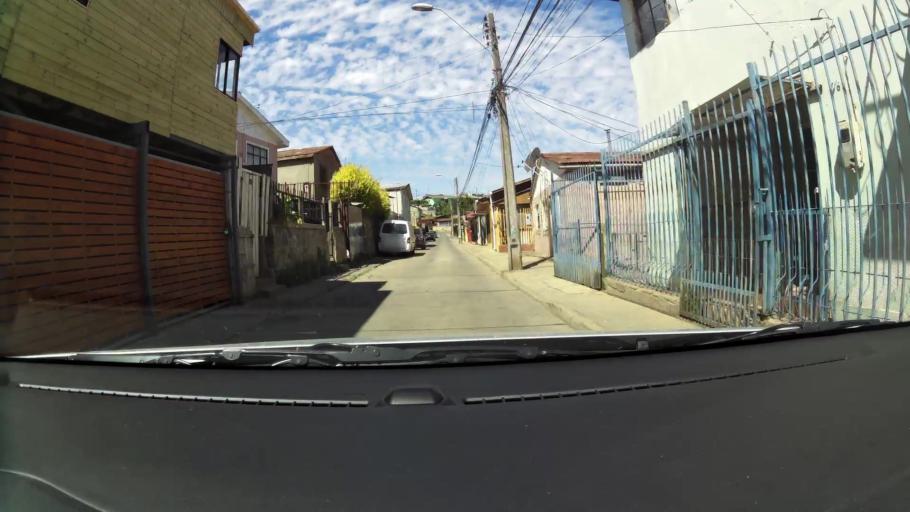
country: CL
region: Valparaiso
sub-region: Provincia de Valparaiso
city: Vina del Mar
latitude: -33.0429
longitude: -71.5802
